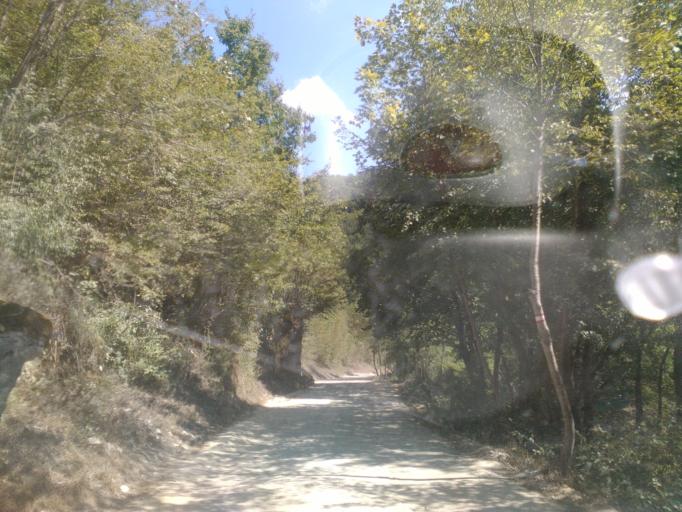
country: BA
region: Federation of Bosnia and Herzegovina
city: Orasac
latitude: 44.6257
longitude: 16.0474
